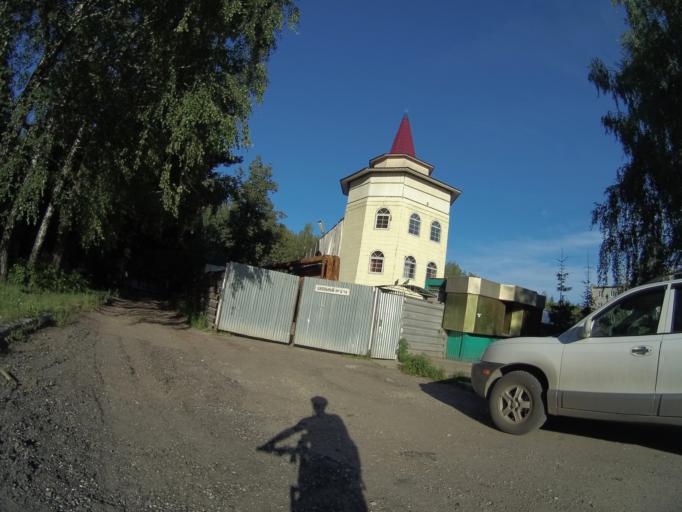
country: RU
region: Vladimir
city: Raduzhnyy
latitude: 56.1011
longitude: 40.2824
